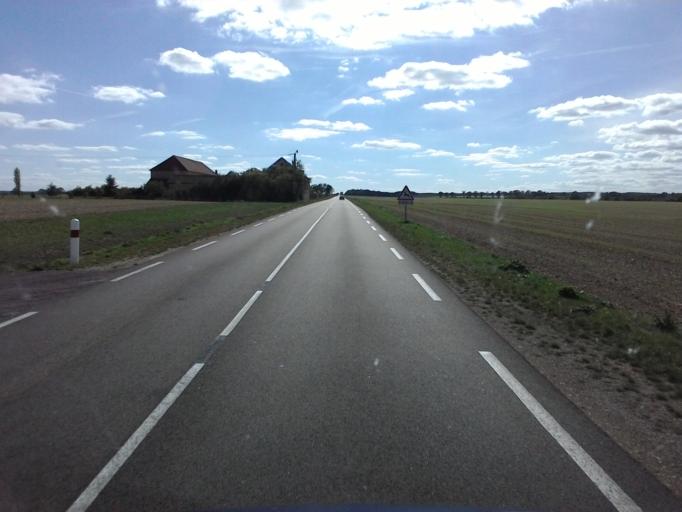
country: FR
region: Bourgogne
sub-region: Departement de la Cote-d'Or
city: Chatillon-sur-Seine
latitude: 47.8510
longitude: 4.5576
